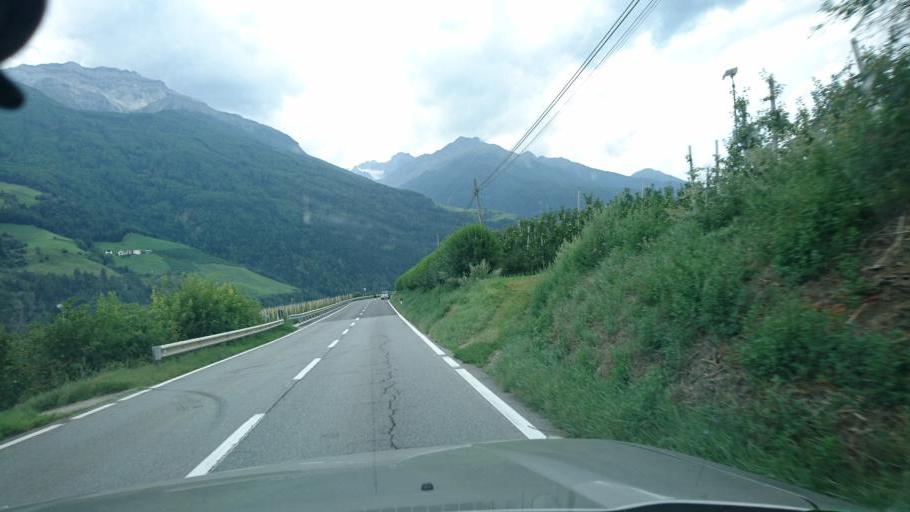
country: IT
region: Trentino-Alto Adige
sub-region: Bolzano
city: Silandro
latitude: 46.6214
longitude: 10.7382
